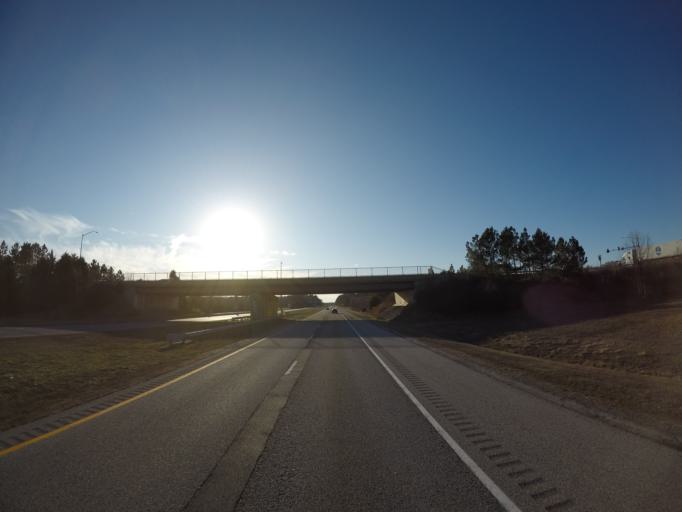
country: US
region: Maryland
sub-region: Queen Anne's County
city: Centreville
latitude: 39.0150
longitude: -76.0756
